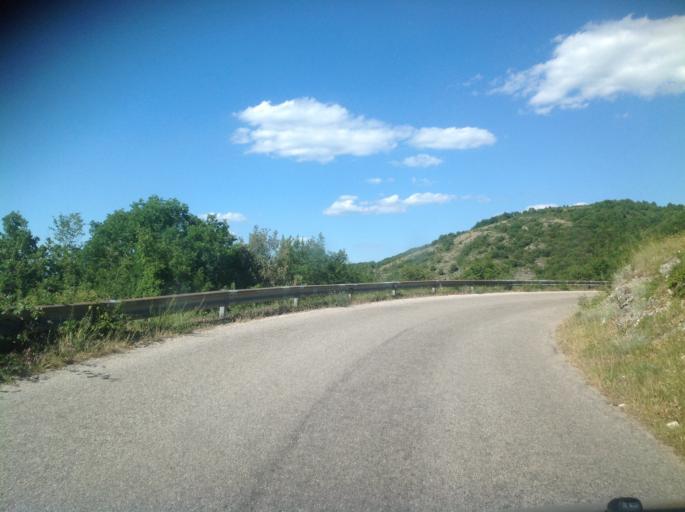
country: IT
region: Umbria
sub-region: Provincia di Terni
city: Stroncone
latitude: 42.4811
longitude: 12.6801
